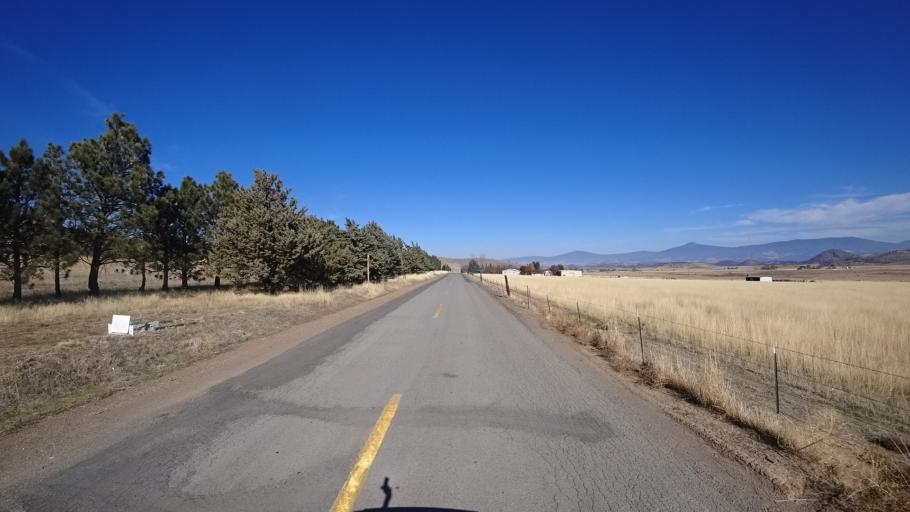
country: US
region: California
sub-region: Siskiyou County
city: Montague
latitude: 41.5913
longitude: -122.5430
